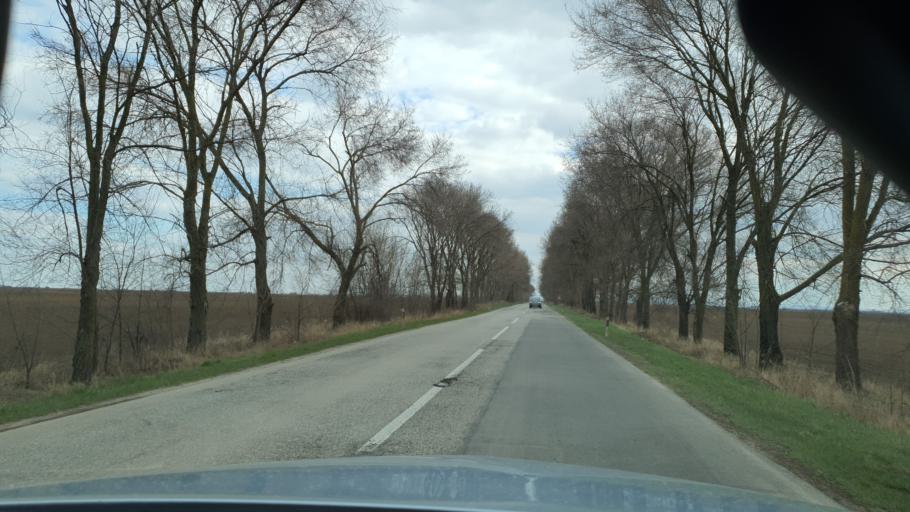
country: RS
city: Obrovac
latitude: 45.4405
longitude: 19.3711
